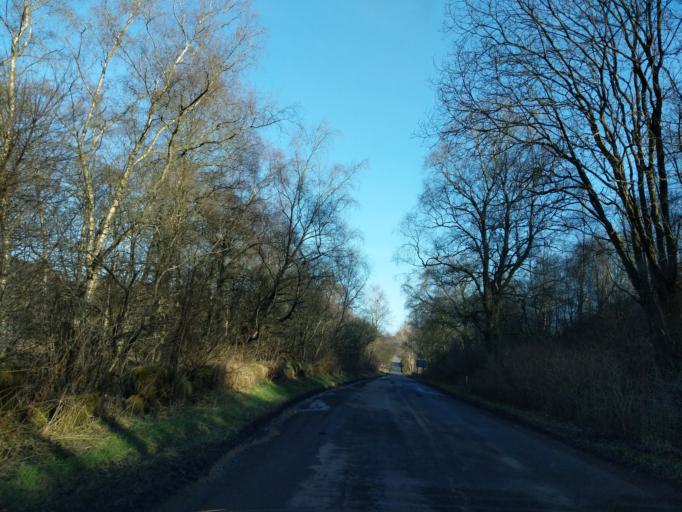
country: GB
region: Scotland
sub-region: The Scottish Borders
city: West Linton
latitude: 55.7196
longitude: -3.4297
